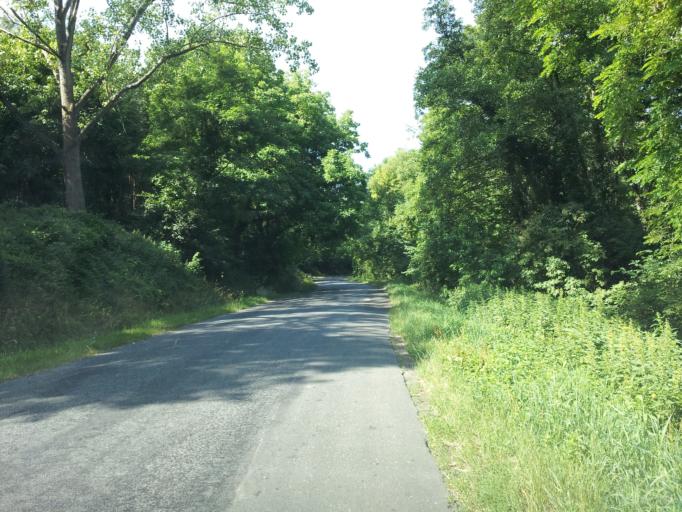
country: HU
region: Zala
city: Heviz
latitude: 46.8649
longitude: 17.1413
